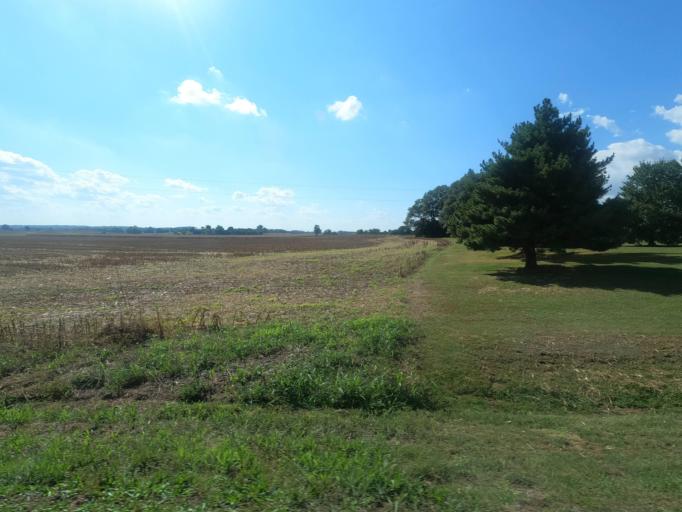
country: US
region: Illinois
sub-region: Massac County
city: Metropolis
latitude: 37.2636
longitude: -88.7611
